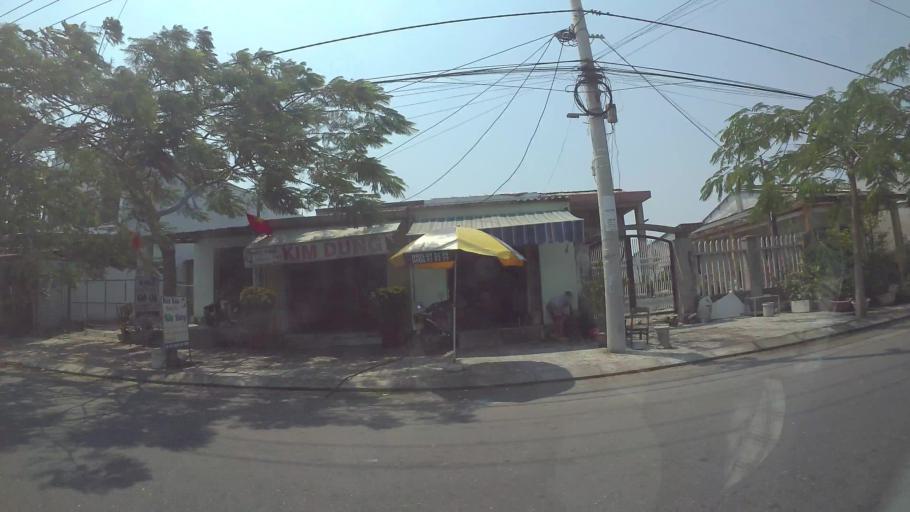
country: VN
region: Da Nang
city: Ngu Hanh Son
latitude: 15.9919
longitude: 108.2664
